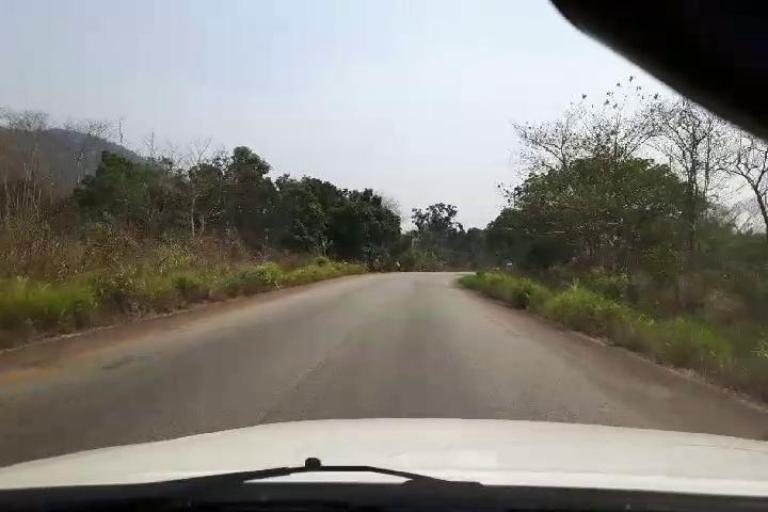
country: SL
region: Northern Province
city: Yonibana
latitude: 8.3813
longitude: -12.1993
